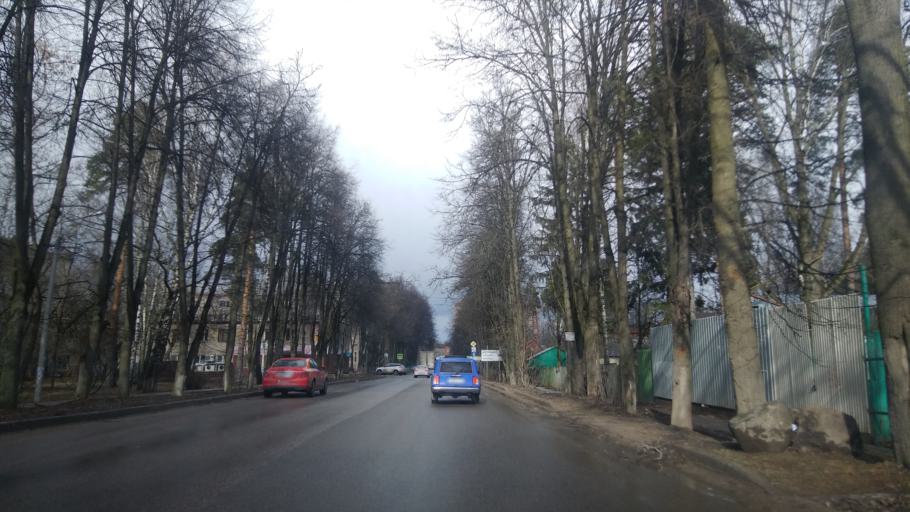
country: RU
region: Moskovskaya
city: Mamontovka
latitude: 56.0074
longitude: 37.8302
